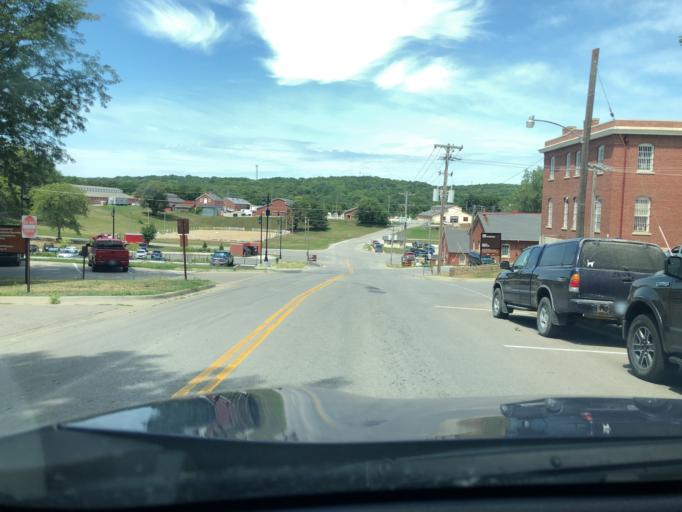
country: US
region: Kansas
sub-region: Leavenworth County
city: Leavenworth
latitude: 39.3582
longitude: -94.9205
